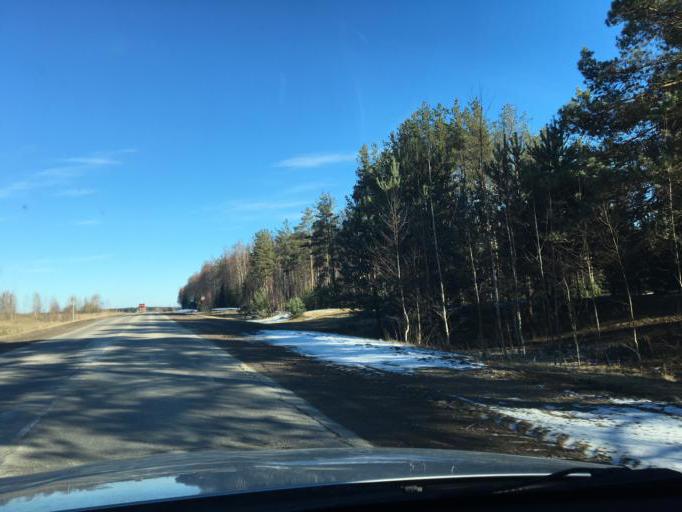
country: LV
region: Jekabpils Rajons
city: Jekabpils
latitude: 56.4861
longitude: 25.8550
